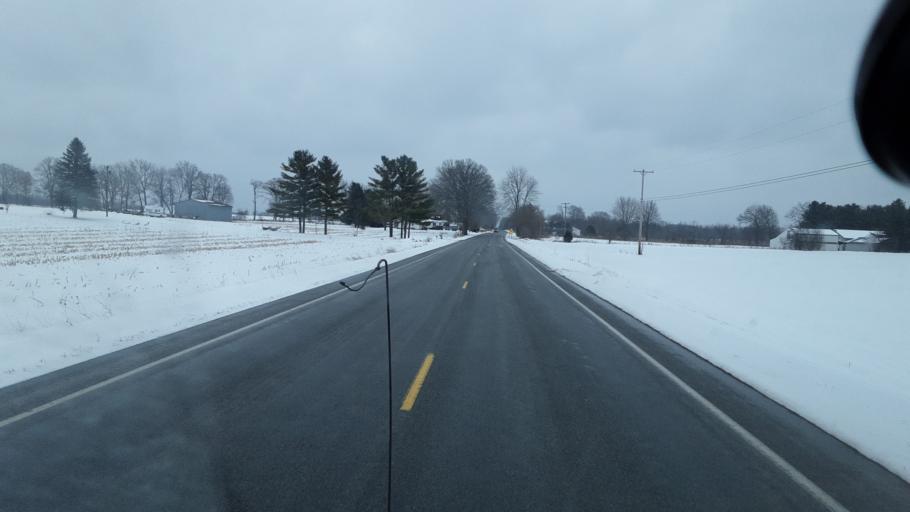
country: US
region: Michigan
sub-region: Ingham County
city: Leslie
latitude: 42.4253
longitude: -84.4136
